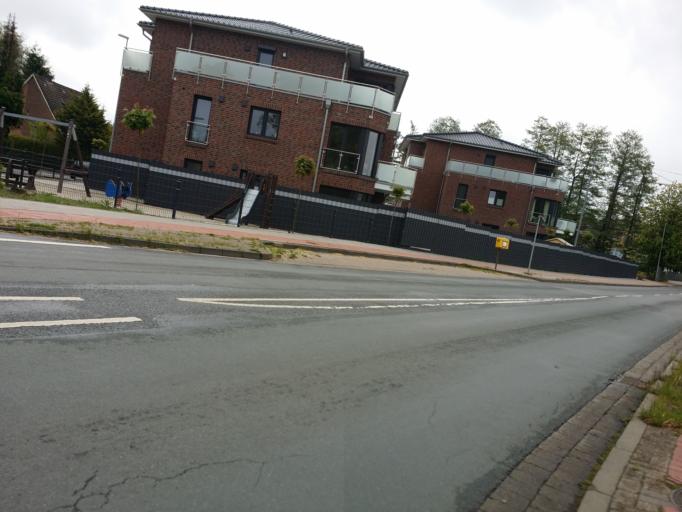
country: DE
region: Lower Saxony
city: Ganderkesee
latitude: 53.0303
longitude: 8.5561
